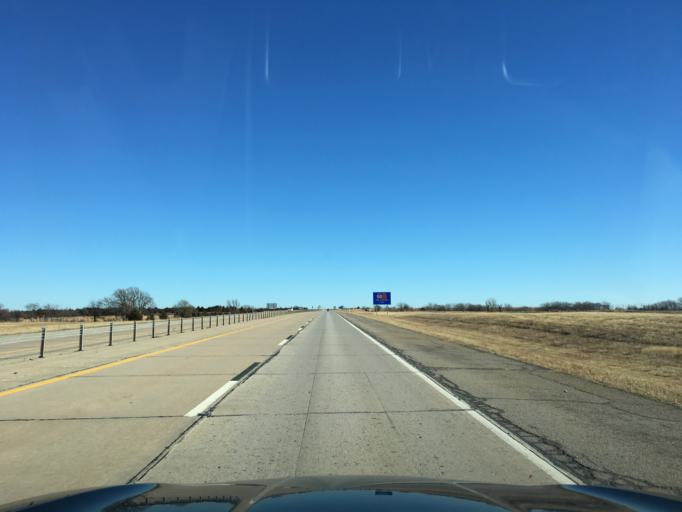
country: US
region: Oklahoma
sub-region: Pawnee County
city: Pawnee
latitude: 36.2247
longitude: -96.8182
